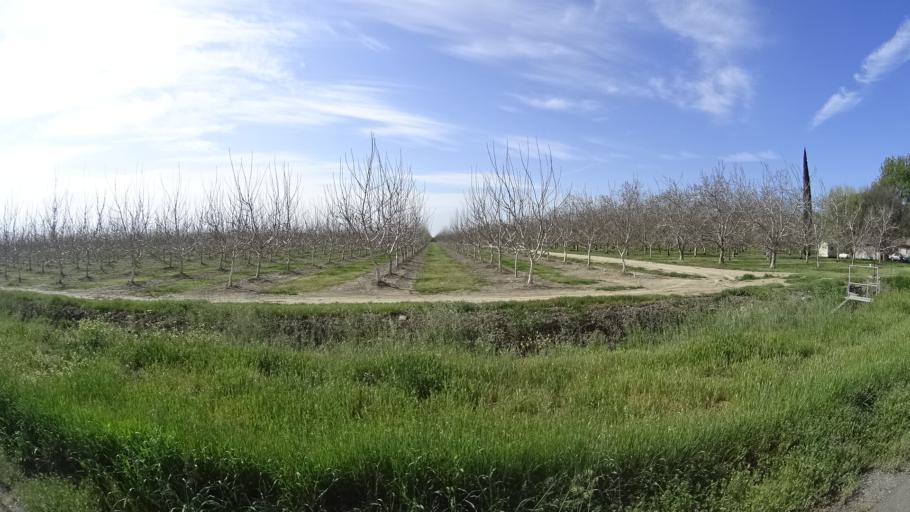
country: US
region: California
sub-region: Glenn County
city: Hamilton City
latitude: 39.6234
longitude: -122.0227
